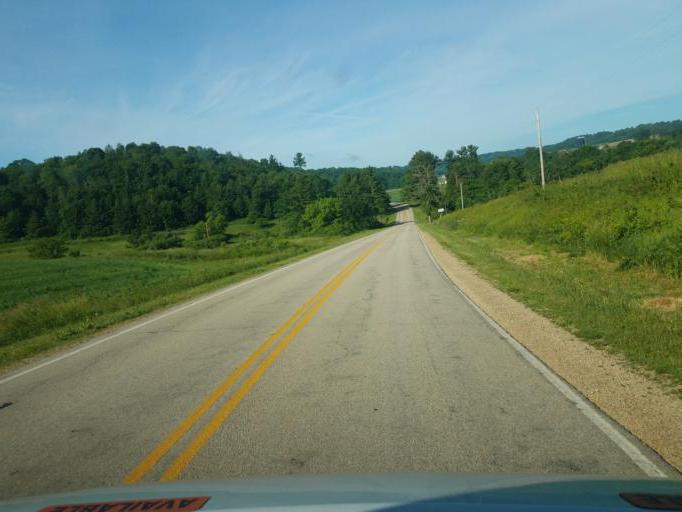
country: US
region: Wisconsin
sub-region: Vernon County
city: Hillsboro
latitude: 43.6136
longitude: -90.2419
